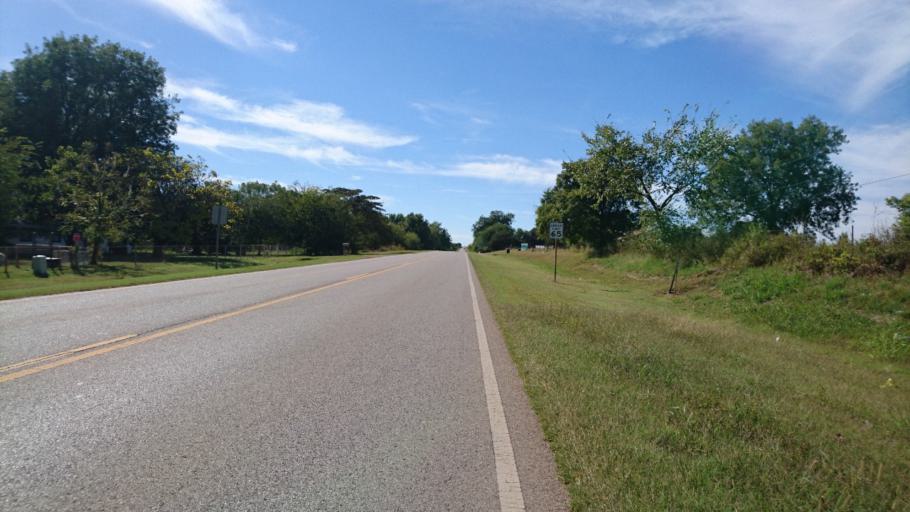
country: US
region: Oklahoma
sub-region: Lincoln County
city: Chandler
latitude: 35.7099
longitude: -96.7725
